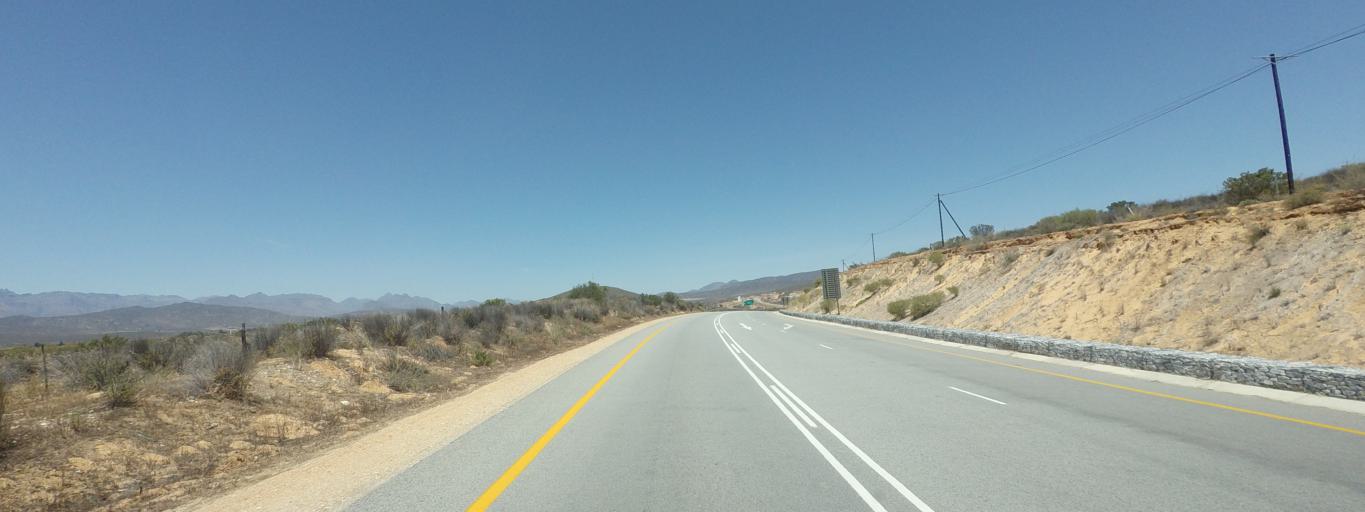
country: ZA
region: Western Cape
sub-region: West Coast District Municipality
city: Clanwilliam
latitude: -32.1633
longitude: 18.8720
